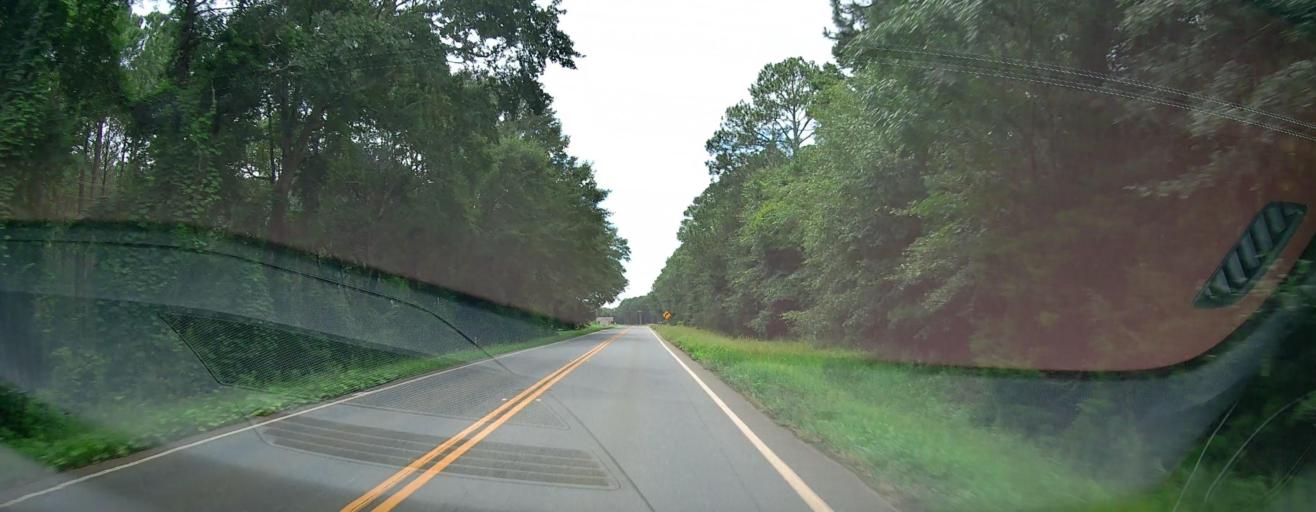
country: US
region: Georgia
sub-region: Schley County
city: Ellaville
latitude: 32.2525
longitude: -84.3945
